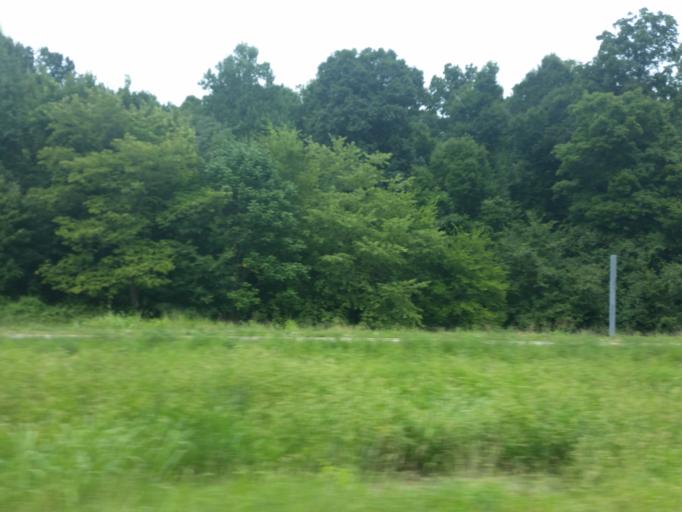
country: US
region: Kentucky
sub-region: Lyon County
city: Eddyville
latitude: 37.0278
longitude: -87.9980
